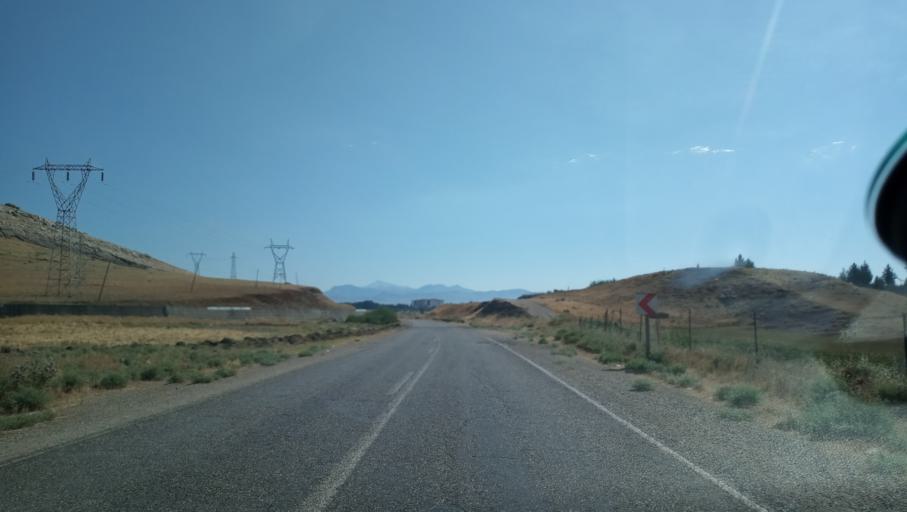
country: TR
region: Diyarbakir
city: Malabadi
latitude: 38.1320
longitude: 41.1851
